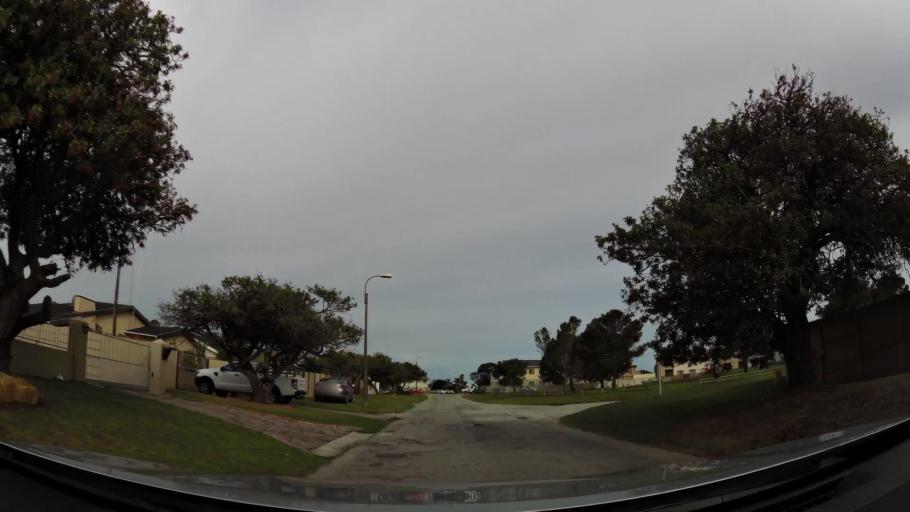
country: ZA
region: Eastern Cape
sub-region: Nelson Mandela Bay Metropolitan Municipality
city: Port Elizabeth
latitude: -33.9389
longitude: 25.4986
